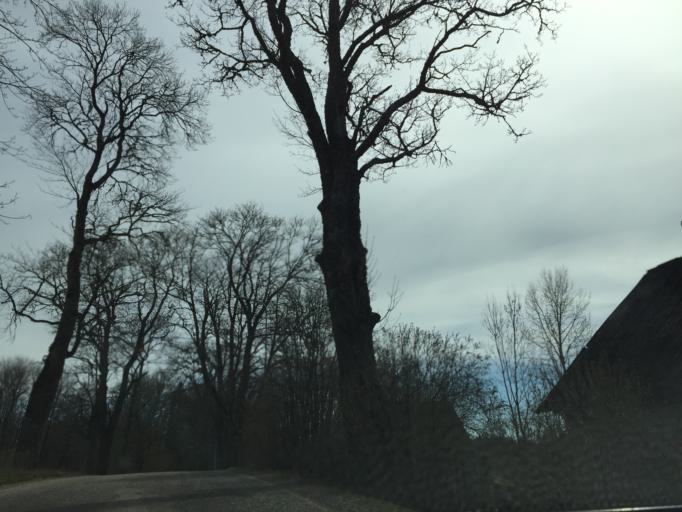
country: LV
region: Strenci
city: Seda
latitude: 57.8153
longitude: 25.8245
